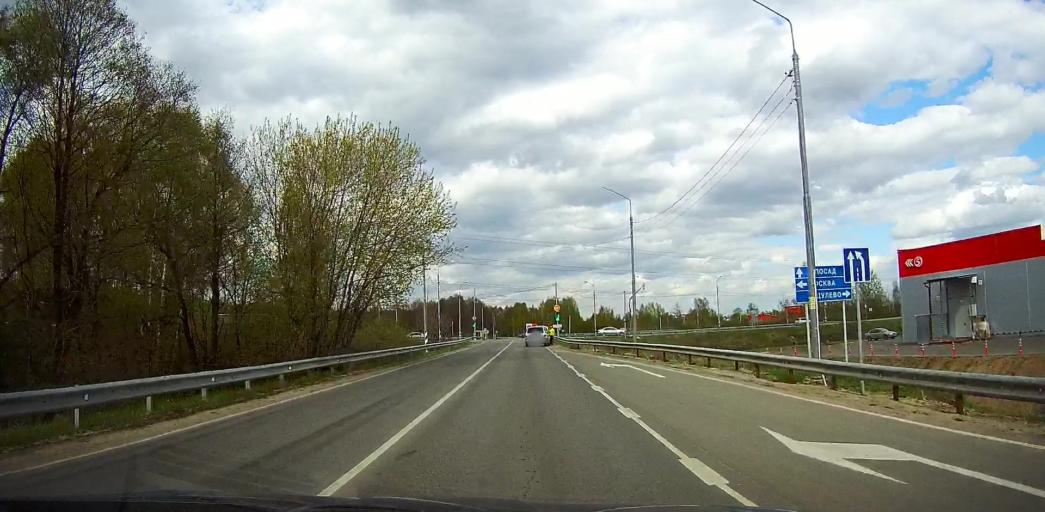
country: RU
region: Moskovskaya
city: Pavlovskiy Posad
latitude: 55.7521
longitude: 38.6538
